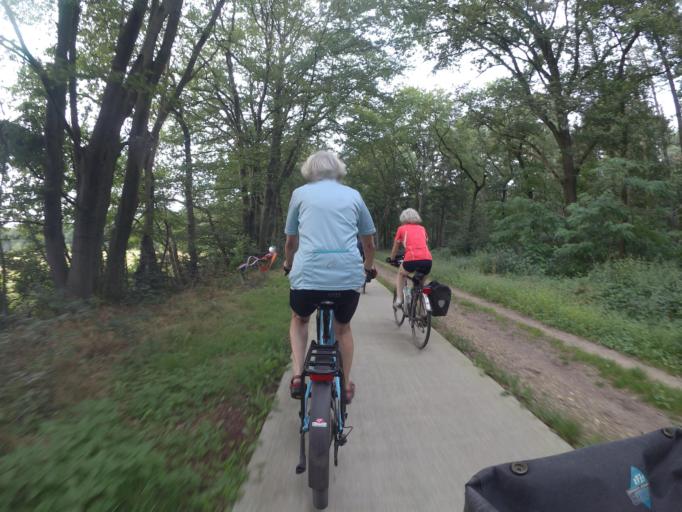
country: NL
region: Gelderland
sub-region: Gemeente Groesbeek
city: Groesbeek
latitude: 51.7696
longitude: 5.9024
